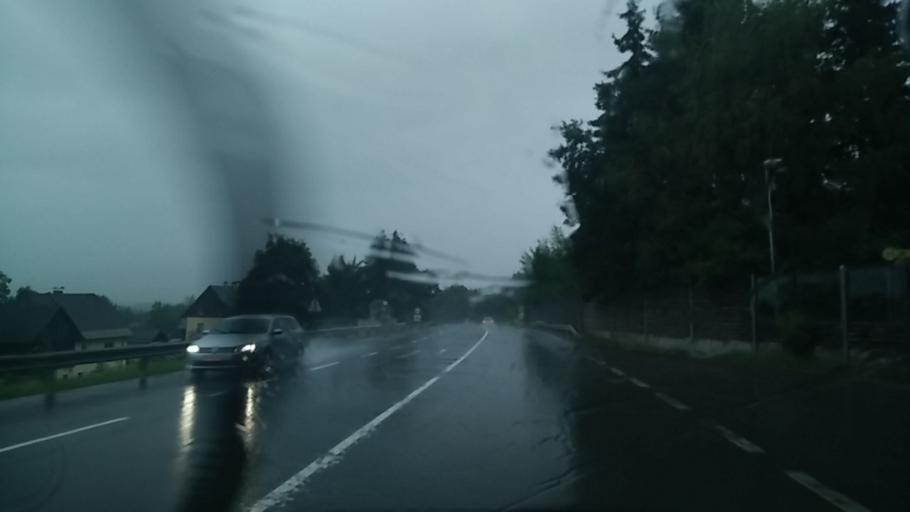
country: AT
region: Carinthia
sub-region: Politischer Bezirk Villach Land
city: Wernberg
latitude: 46.6254
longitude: 13.9297
